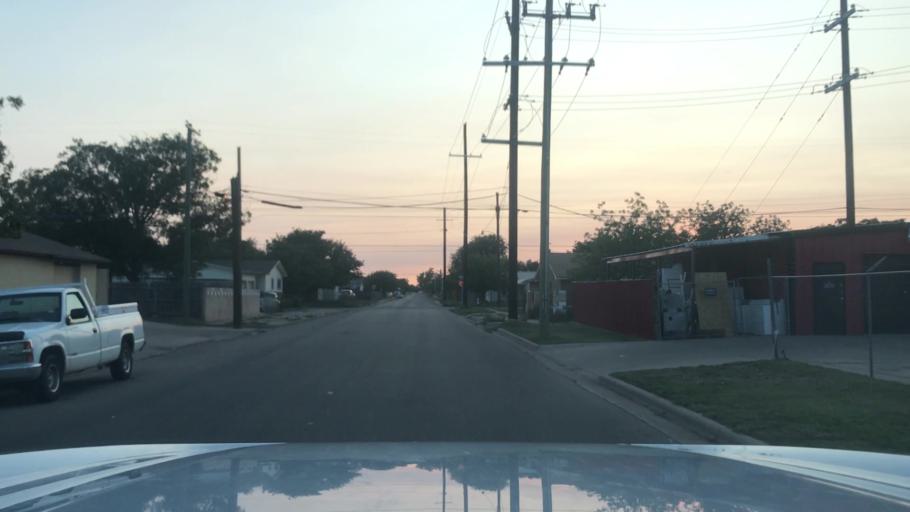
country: US
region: Texas
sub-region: Lubbock County
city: Lubbock
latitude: 33.5979
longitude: -101.8608
